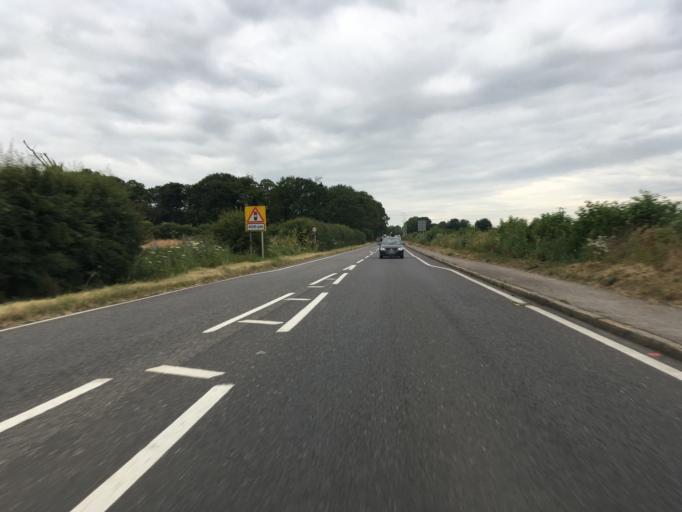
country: GB
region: England
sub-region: Central Bedfordshire
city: Kensworth
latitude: 51.8663
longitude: -0.4890
